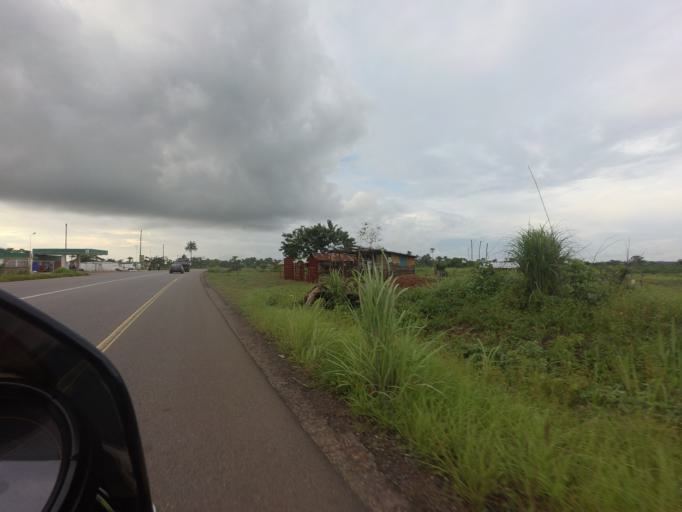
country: SL
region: Northern Province
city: Kambia
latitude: 9.0596
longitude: -12.9168
